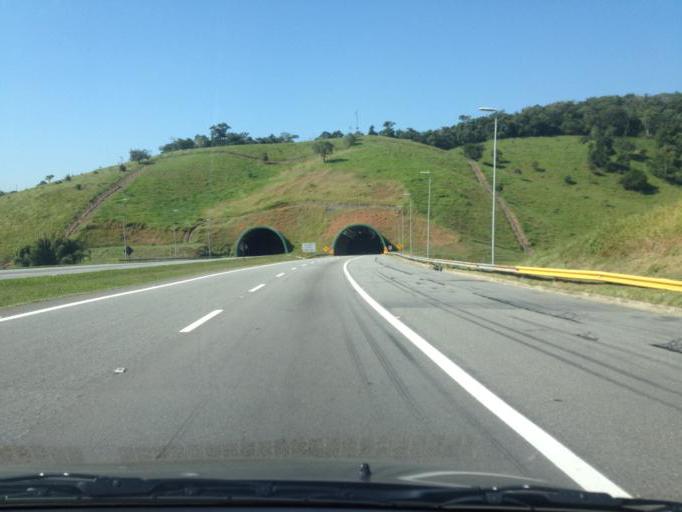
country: BR
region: Sao Paulo
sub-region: Jacarei
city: Jacarei
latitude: -23.3457
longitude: -45.9996
